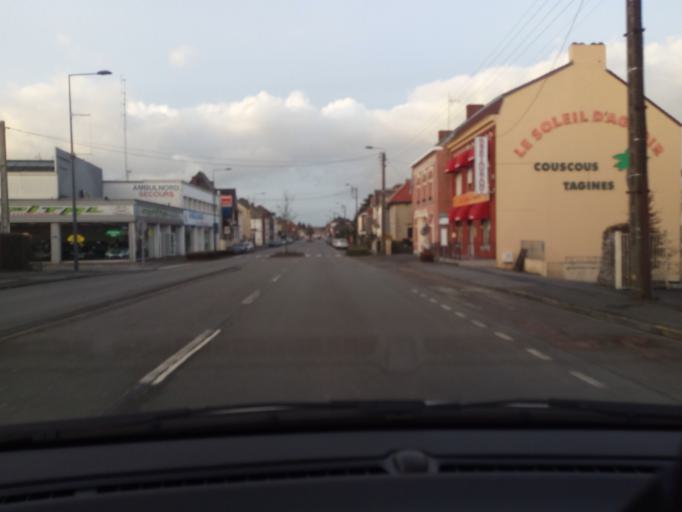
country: FR
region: Nord-Pas-de-Calais
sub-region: Departement du Nord
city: Maubeuge
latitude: 50.2838
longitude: 3.9749
